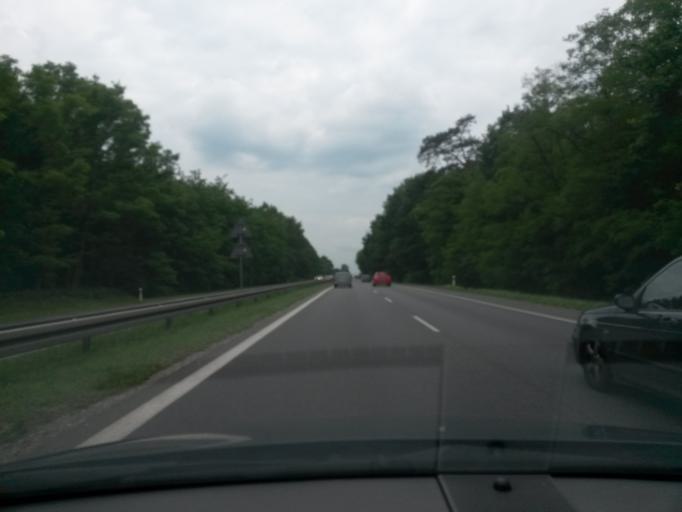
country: PL
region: Lodz Voivodeship
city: Zabia Wola
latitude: 52.0593
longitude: 20.7347
